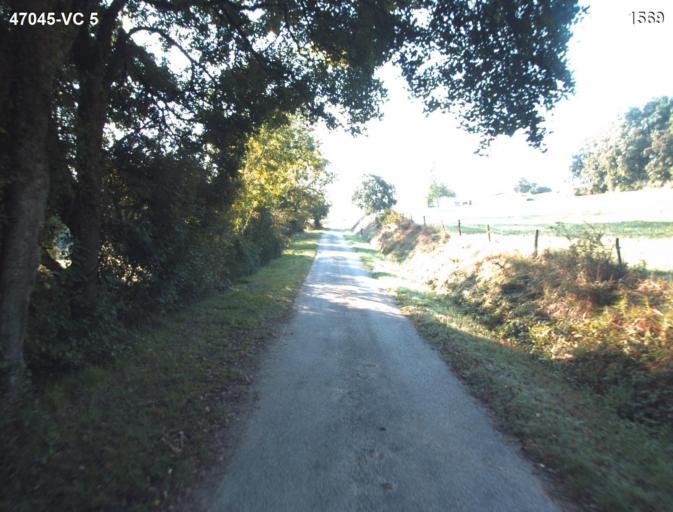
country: FR
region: Aquitaine
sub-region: Departement du Lot-et-Garonne
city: Nerac
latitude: 44.1433
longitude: 0.4045
